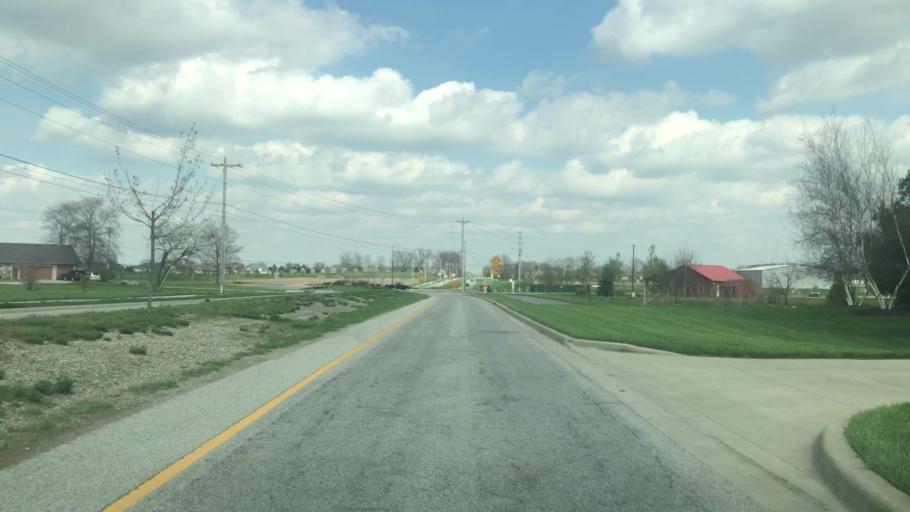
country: US
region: Indiana
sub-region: Johnson County
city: Waterloo
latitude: 39.5477
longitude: -86.1989
